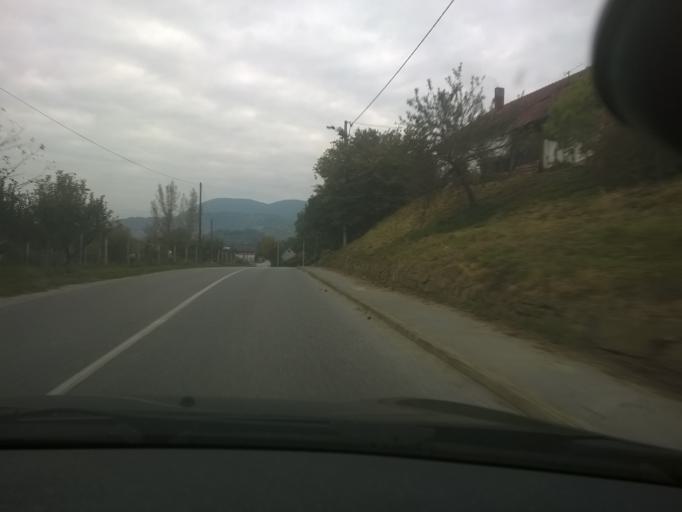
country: HR
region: Krapinsko-Zagorska
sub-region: Grad Krapina
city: Krapina
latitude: 46.1404
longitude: 15.8811
